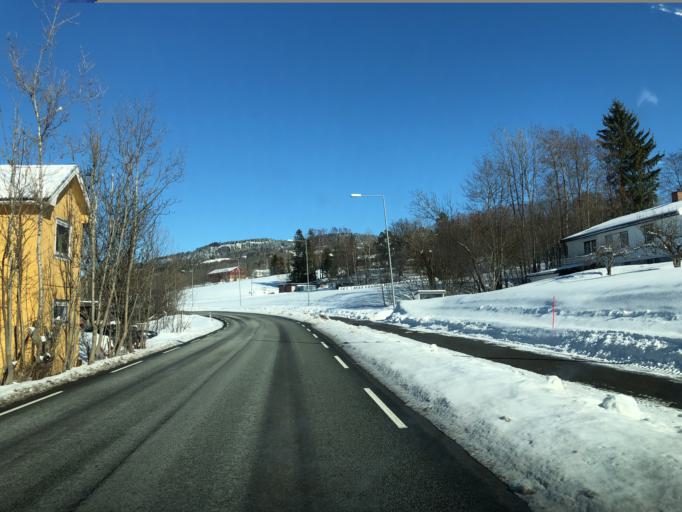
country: NO
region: Buskerud
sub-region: Lier
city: Tranby
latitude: 59.8180
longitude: 10.2510
